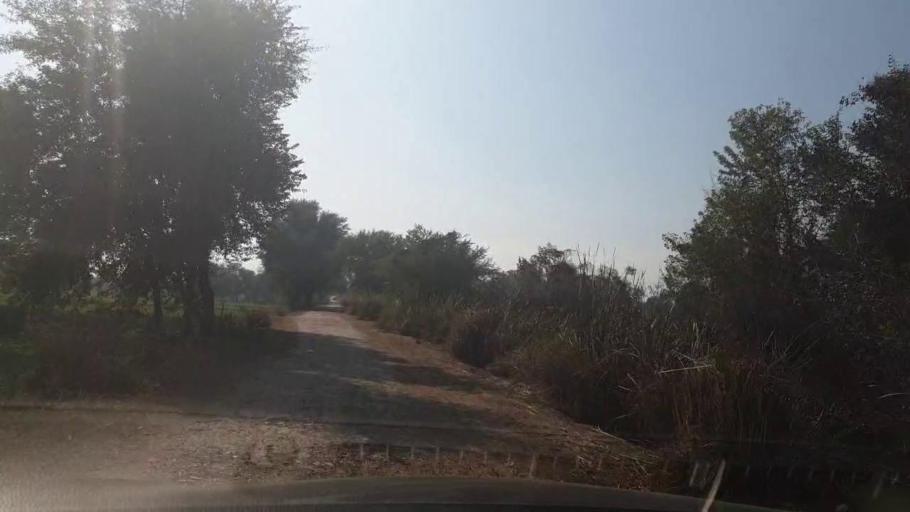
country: PK
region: Sindh
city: Ubauro
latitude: 28.1394
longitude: 69.6845
